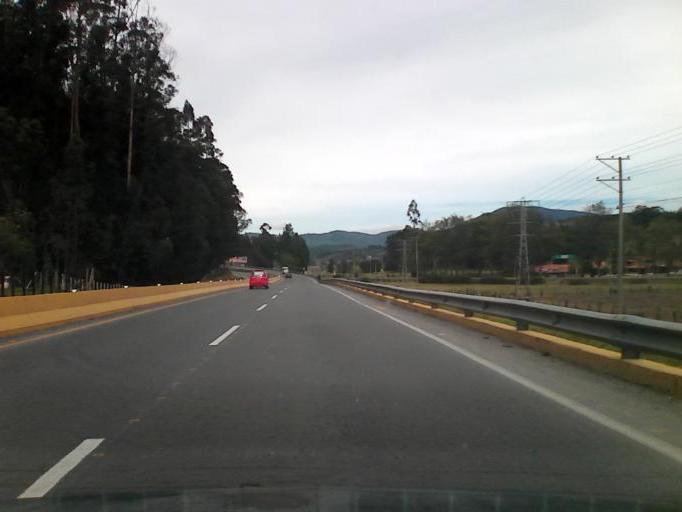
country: CO
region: Boyaca
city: Duitama
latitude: 5.7921
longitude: -73.0475
